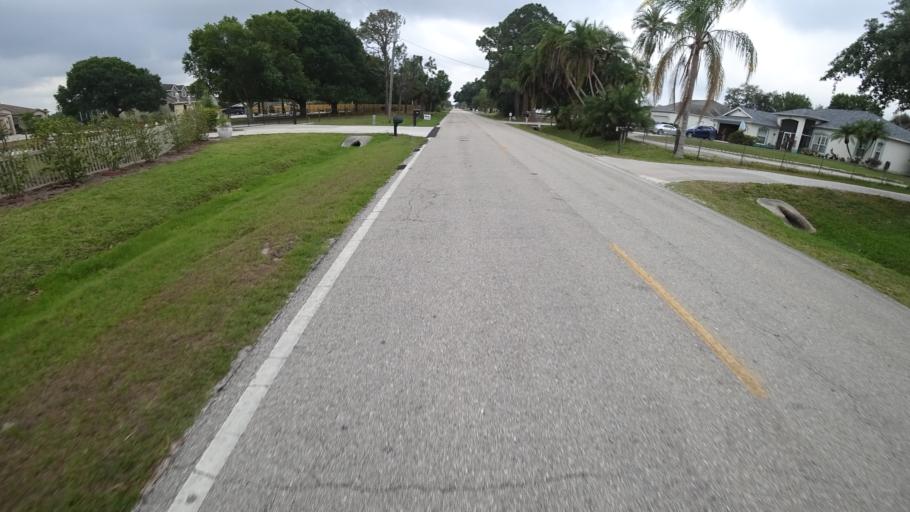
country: US
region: Florida
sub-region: Manatee County
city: Samoset
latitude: 27.4597
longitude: -82.5162
